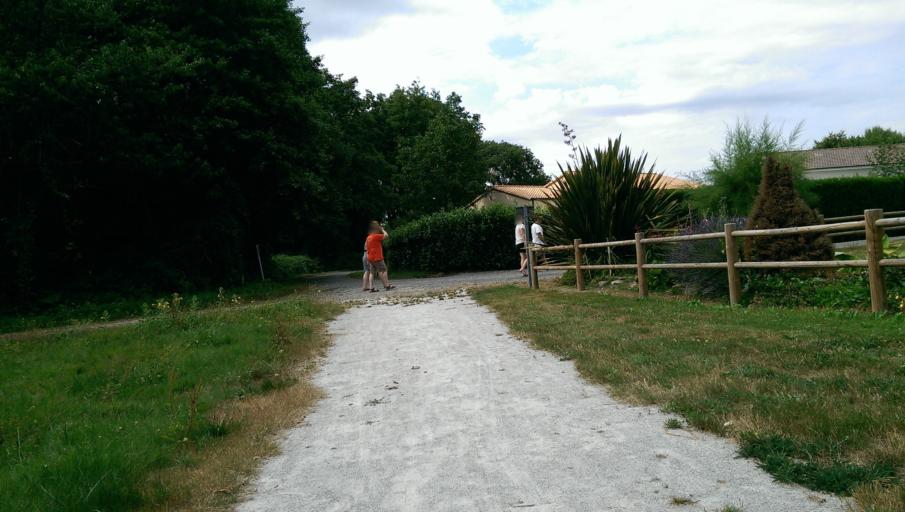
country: FR
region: Pays de la Loire
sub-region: Departement de la Loire-Atlantique
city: La Planche
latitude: 47.0126
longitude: -1.4337
